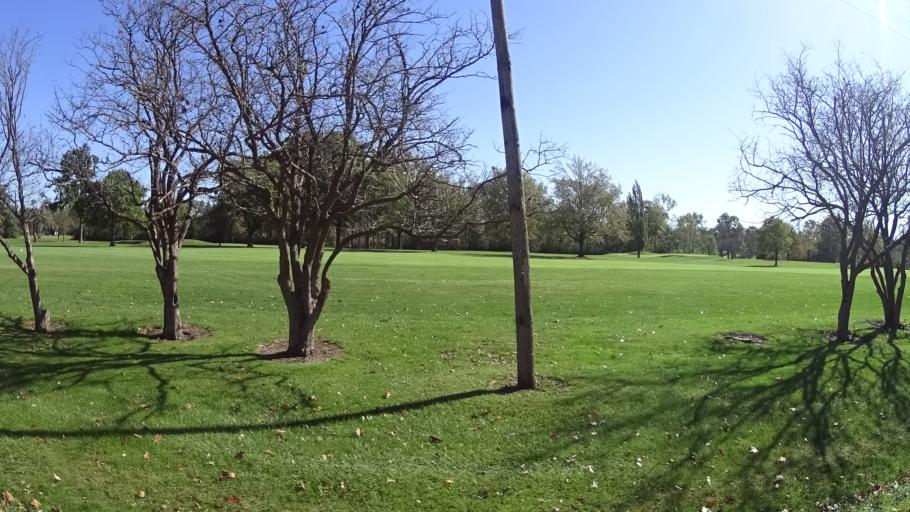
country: US
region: Ohio
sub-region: Lorain County
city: Oberlin
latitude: 41.2837
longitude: -82.2387
